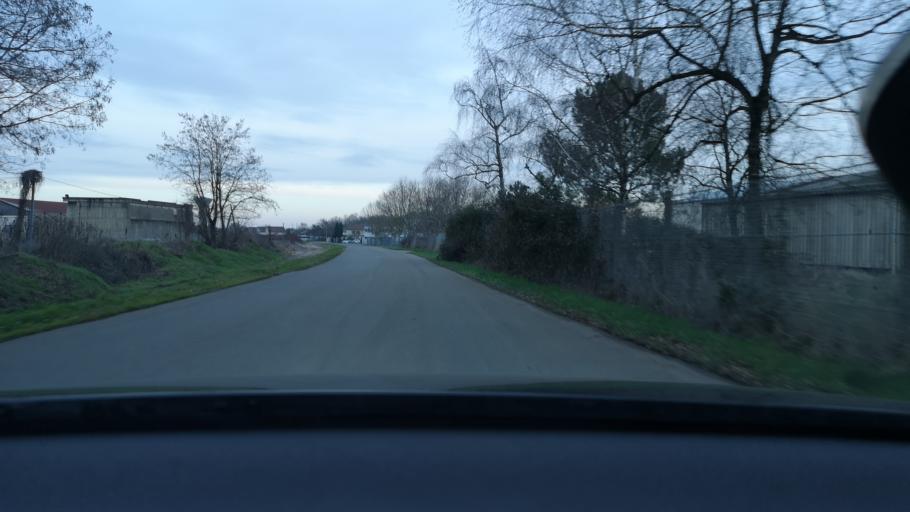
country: FR
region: Bourgogne
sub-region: Departement de Saone-et-Loire
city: Chalon-sur-Saone
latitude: 46.7718
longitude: 4.8498
